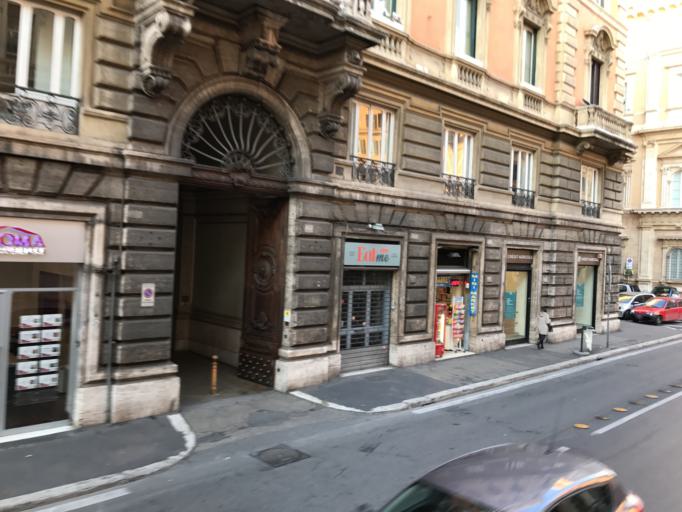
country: VA
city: Vatican City
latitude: 41.8975
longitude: 12.4696
